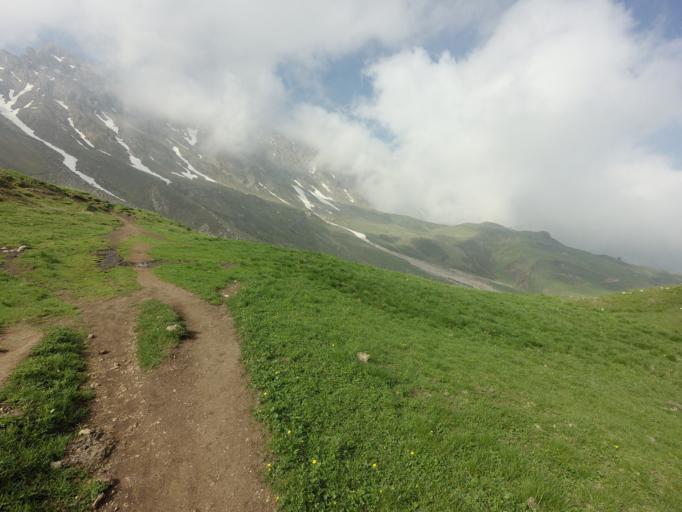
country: IT
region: Trentino-Alto Adige
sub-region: Bolzano
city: Ortisei
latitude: 46.5094
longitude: 11.6347
